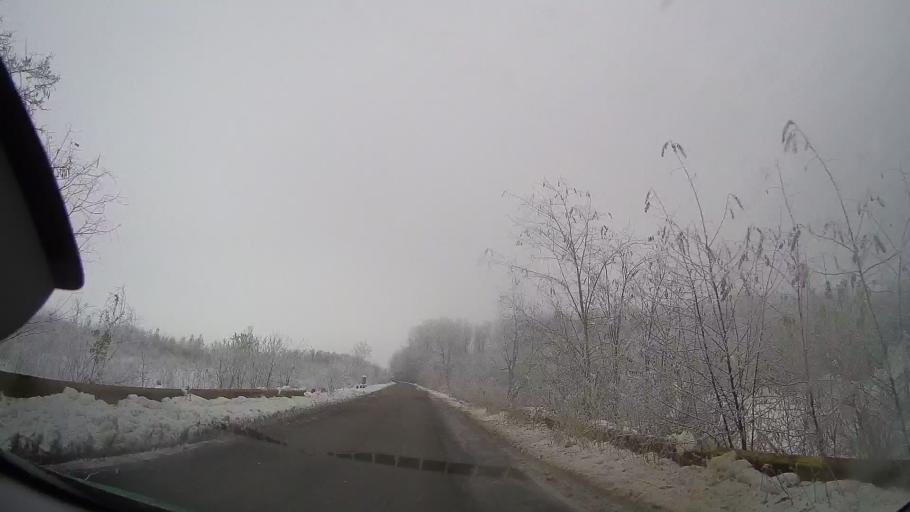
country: RO
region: Neamt
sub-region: Comuna Horia
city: Cotu Vames
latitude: 46.8849
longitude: 26.9697
